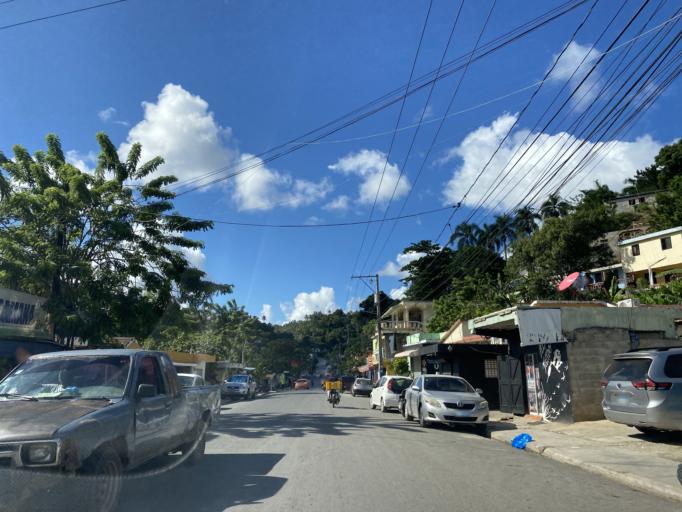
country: DO
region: Samana
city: Samana
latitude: 19.2053
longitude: -69.3451
